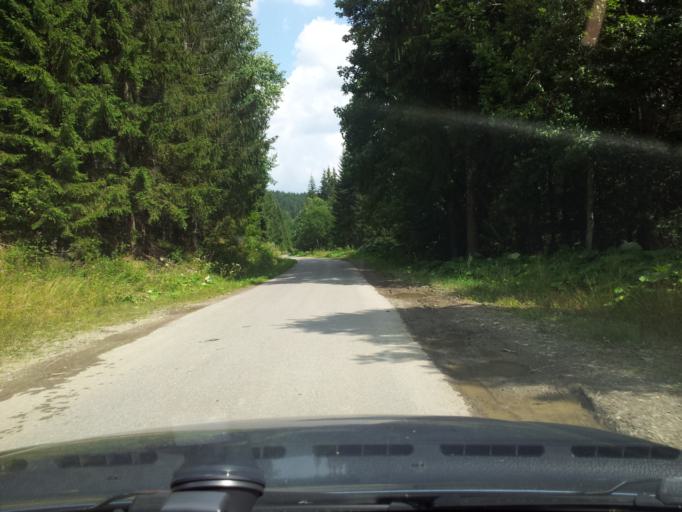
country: SK
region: Zilinsky
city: Oravska Lesna
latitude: 49.3891
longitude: 19.2074
